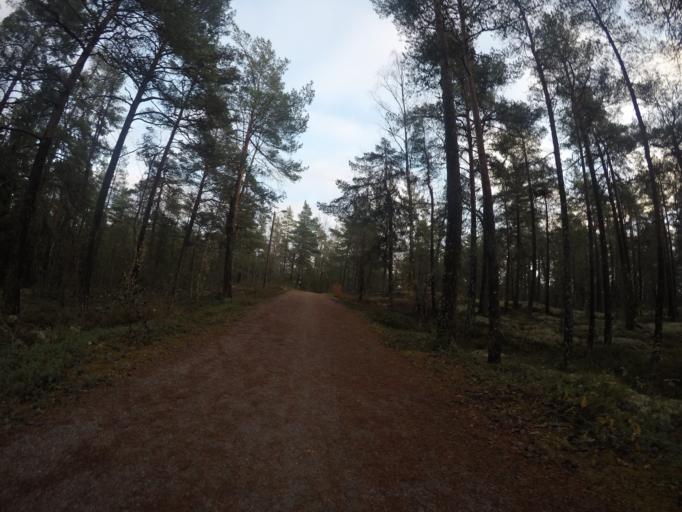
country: SE
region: Soedermanland
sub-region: Eskilstuna Kommun
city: Eskilstuna
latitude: 59.3438
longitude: 16.5214
